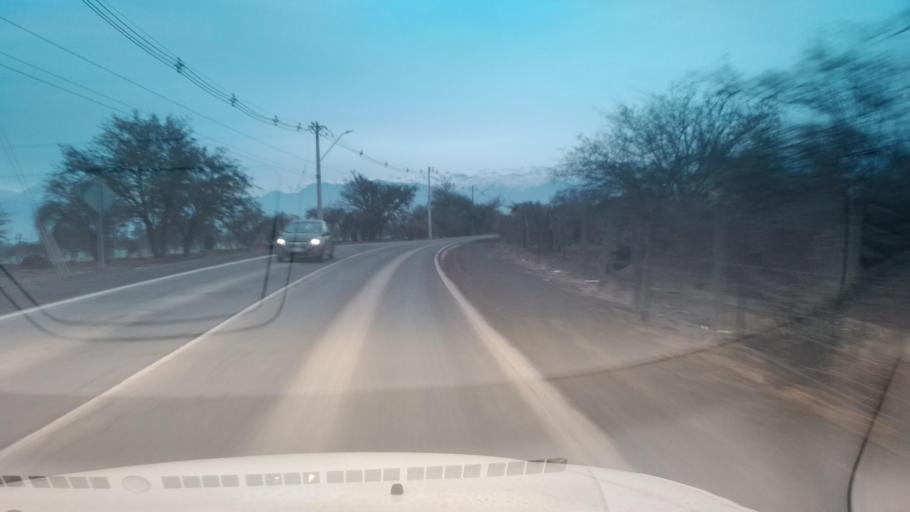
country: CL
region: Santiago Metropolitan
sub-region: Provincia de Chacabuco
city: Chicureo Abajo
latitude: -33.0920
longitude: -70.7395
